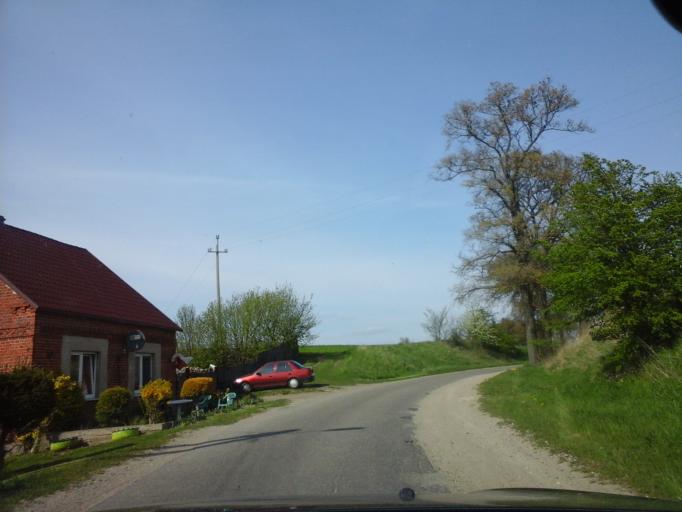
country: PL
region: West Pomeranian Voivodeship
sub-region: Powiat choszczenski
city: Krzecin
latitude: 53.0397
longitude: 15.5439
